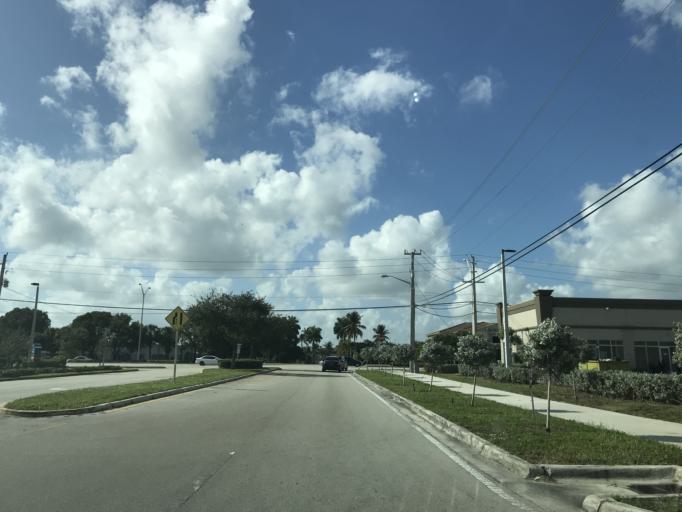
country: US
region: Florida
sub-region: Broward County
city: Margate
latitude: 26.2656
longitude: -80.2007
